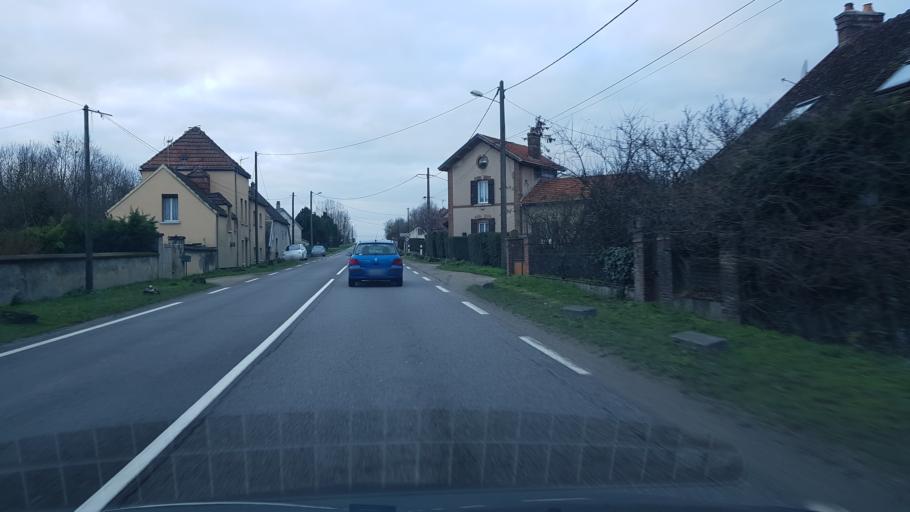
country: FR
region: Champagne-Ardenne
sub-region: Departement de la Marne
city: Esternay
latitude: 48.7134
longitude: 3.4858
